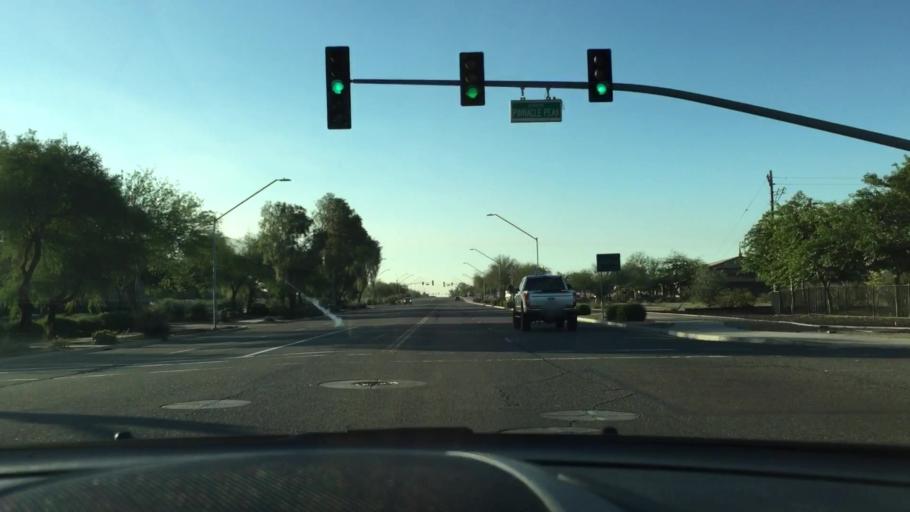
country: US
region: Arizona
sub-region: Maricopa County
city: Sun City
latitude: 33.6959
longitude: -112.2031
